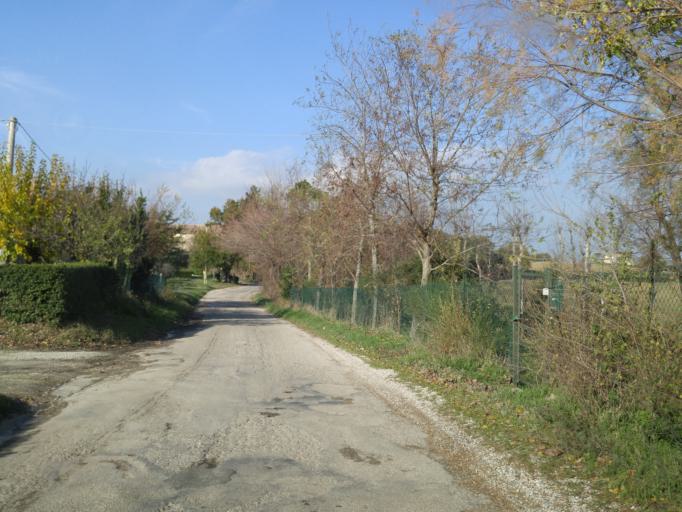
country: IT
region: The Marches
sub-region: Provincia di Pesaro e Urbino
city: Lucrezia
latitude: 43.8095
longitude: 12.9112
